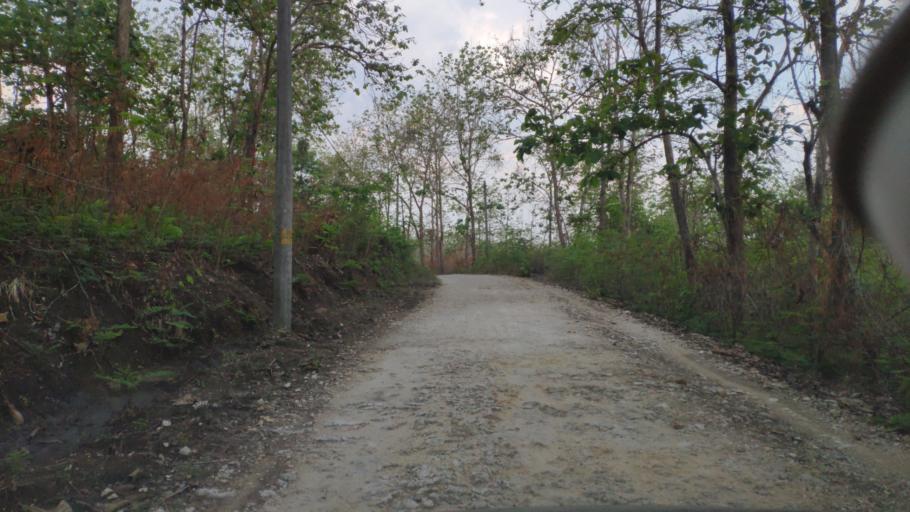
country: ID
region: Central Java
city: Semanggi
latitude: -7.0660
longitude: 111.4292
